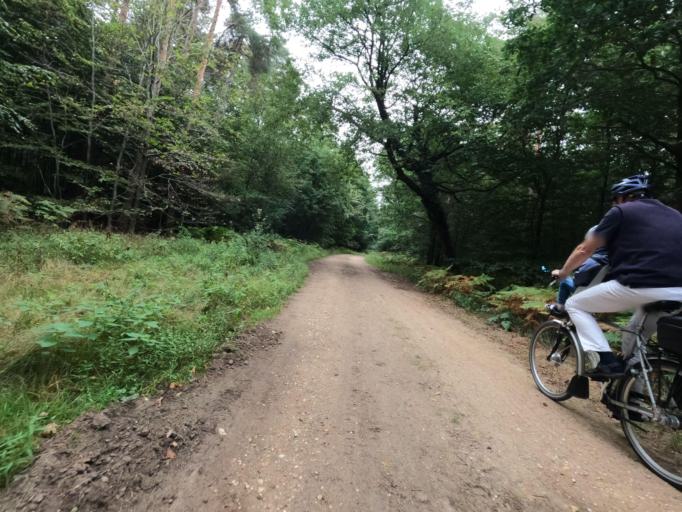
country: DE
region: North Rhine-Westphalia
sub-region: Regierungsbezirk Dusseldorf
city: Niederkruchten
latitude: 51.1766
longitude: 6.1737
